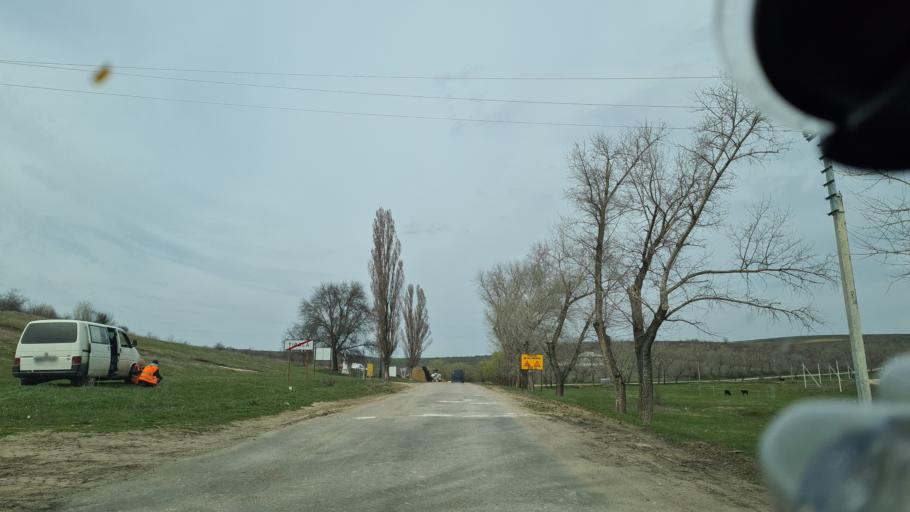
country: MD
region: Chisinau
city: Singera
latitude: 46.8396
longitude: 28.9794
